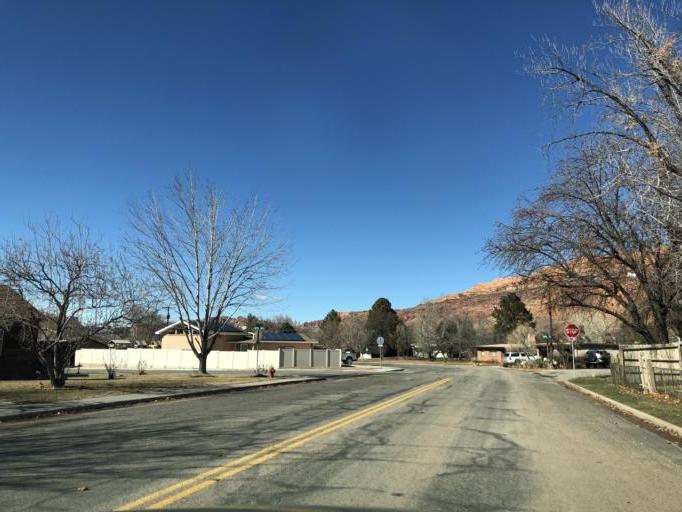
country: US
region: Utah
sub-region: Grand County
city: Moab
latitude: 38.5821
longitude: -109.5546
